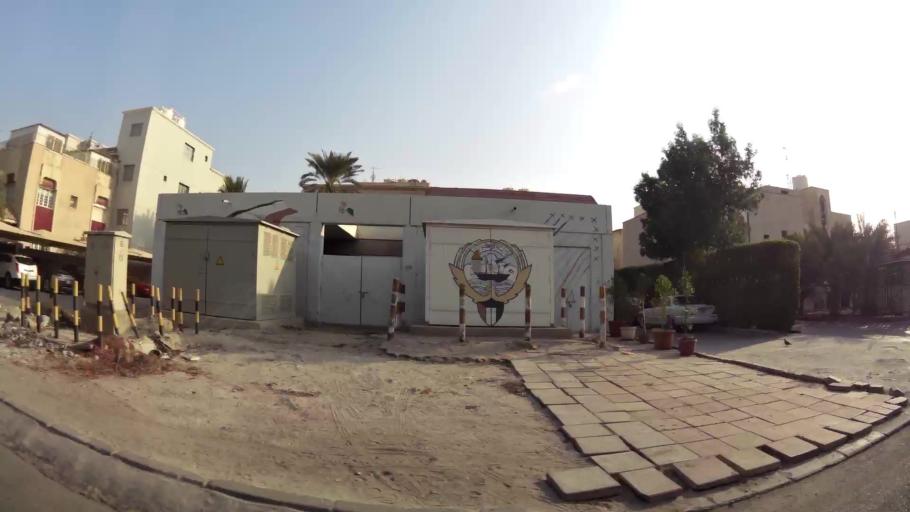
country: KW
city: Bayan
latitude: 29.3013
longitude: 48.0484
